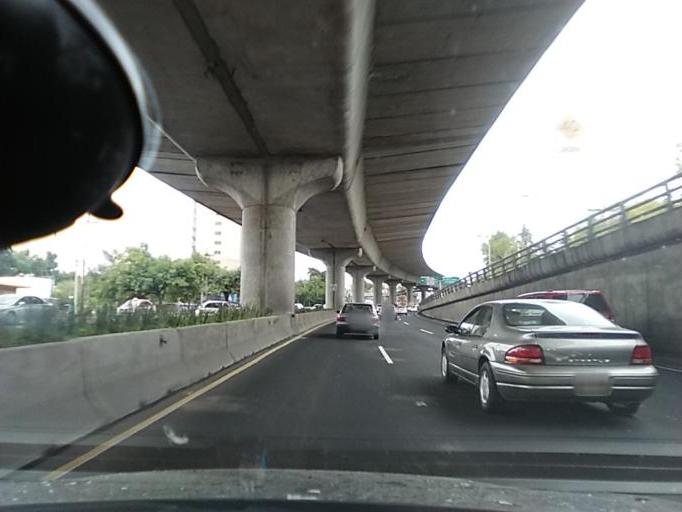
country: MX
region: Mexico City
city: Magdalena Contreras
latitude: 19.3278
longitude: -99.2122
